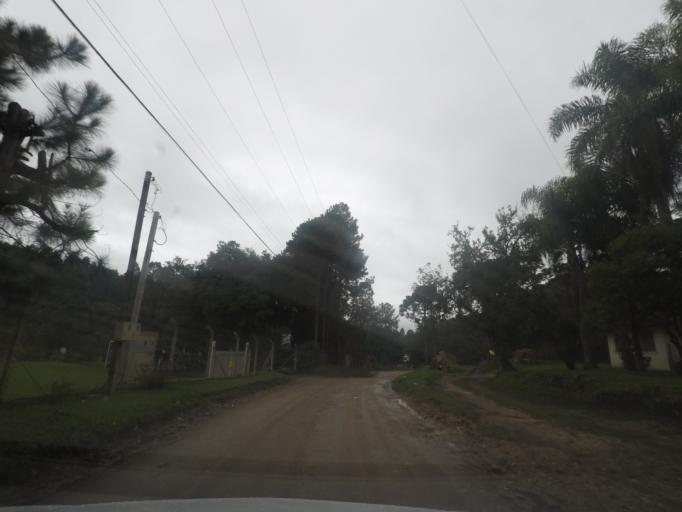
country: BR
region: Parana
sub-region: Campina Grande Do Sul
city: Campina Grande do Sul
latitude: -25.3045
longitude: -49.1210
